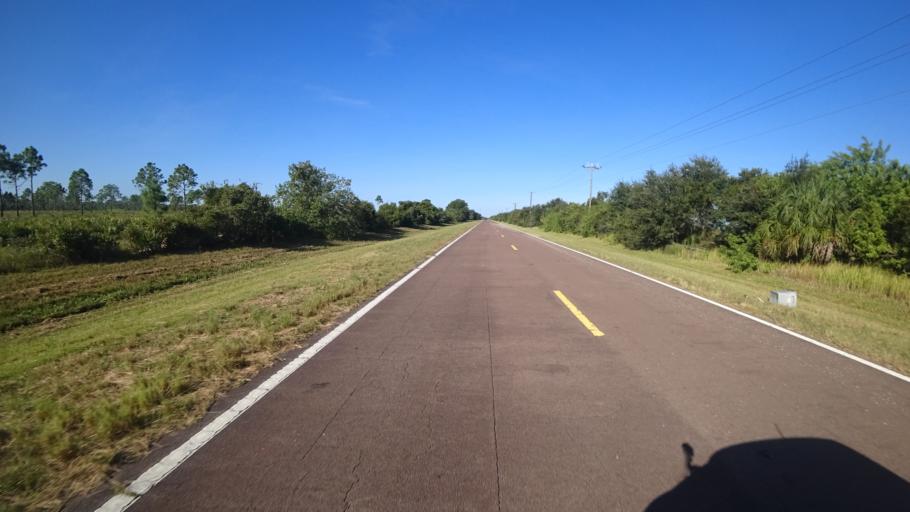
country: US
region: Florida
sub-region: Hillsborough County
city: Ruskin
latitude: 27.6539
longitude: -82.4759
